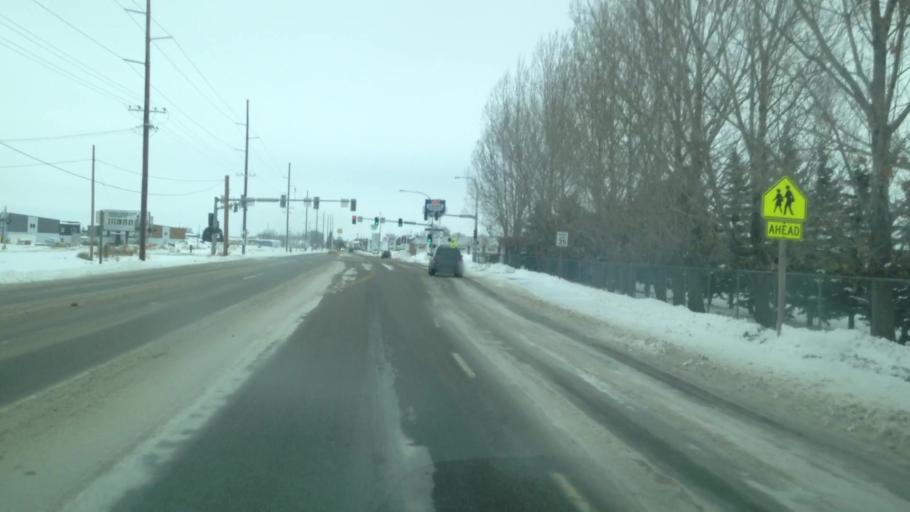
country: US
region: Idaho
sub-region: Madison County
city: Rexburg
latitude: 43.8107
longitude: -111.8032
